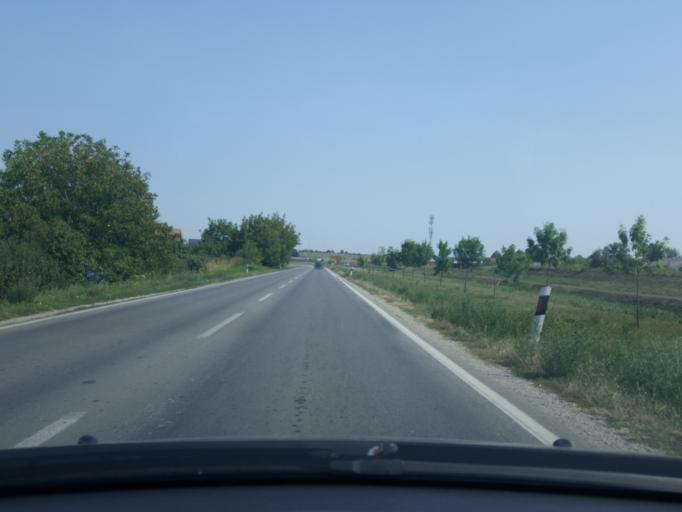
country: RS
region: Central Serbia
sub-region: Macvanski Okrug
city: Sabac
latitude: 44.7426
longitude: 19.6720
